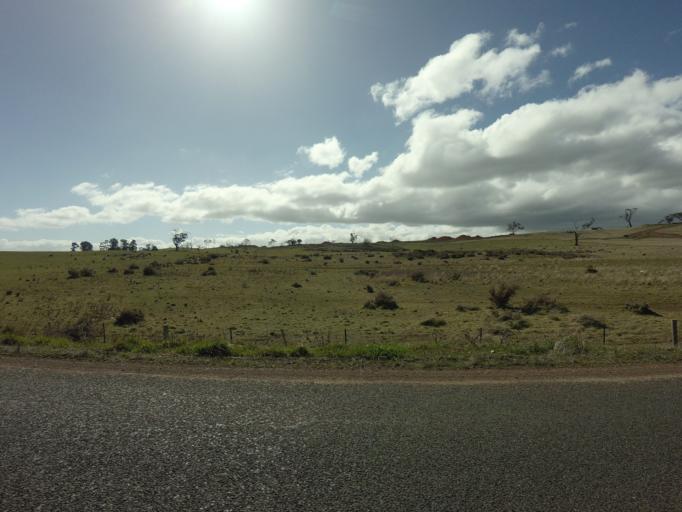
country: AU
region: Tasmania
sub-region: Northern Midlands
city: Evandale
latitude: -41.9026
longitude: 147.4481
